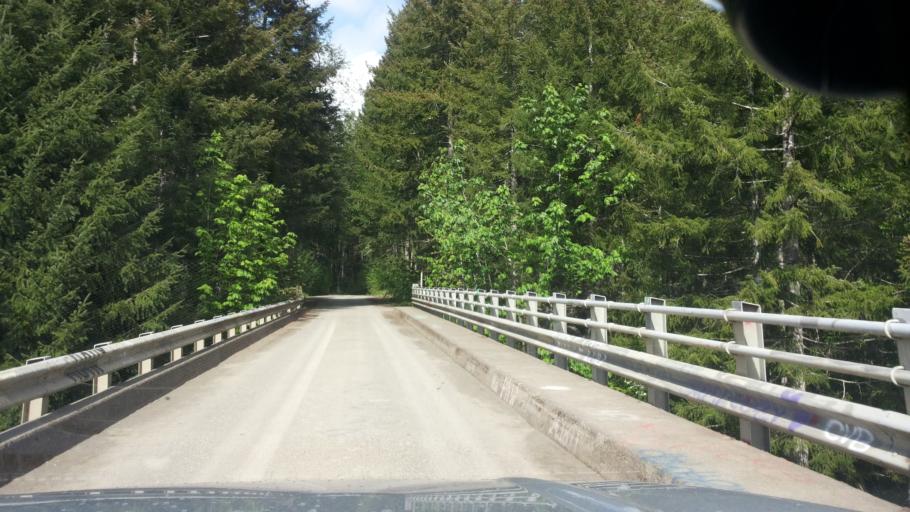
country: US
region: Washington
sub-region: Mason County
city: Shelton
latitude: 47.3684
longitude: -123.2796
